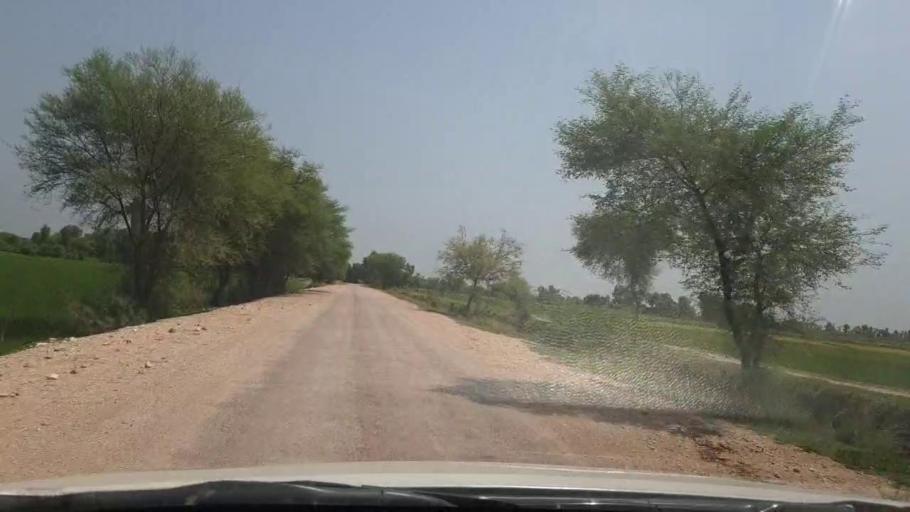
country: PK
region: Sindh
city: Rustam jo Goth
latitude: 28.0290
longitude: 68.7588
